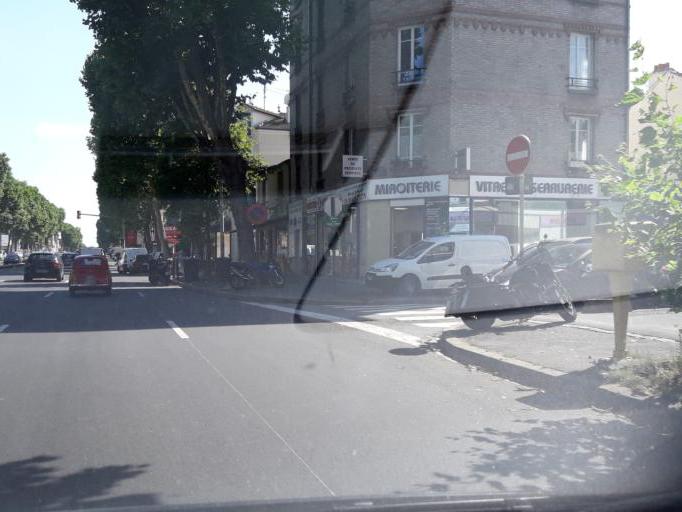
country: FR
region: Ile-de-France
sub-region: Departement du Val-de-Marne
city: Arcueil
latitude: 48.7996
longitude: 2.3230
